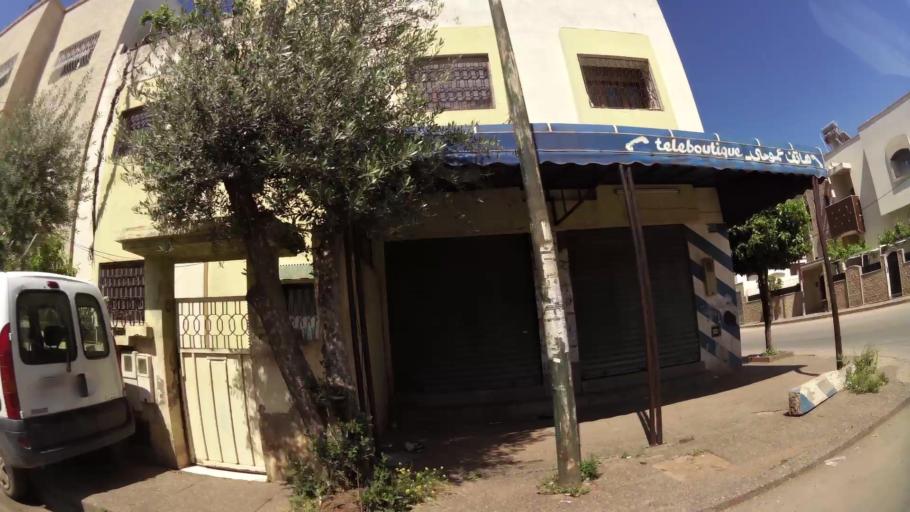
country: MA
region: Fes-Boulemane
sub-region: Fes
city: Fes
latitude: 34.0193
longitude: -5.0255
